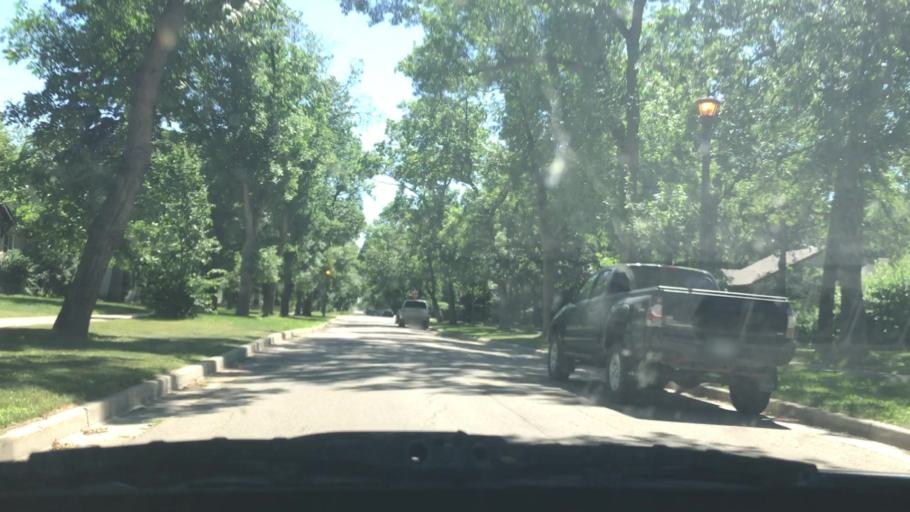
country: CA
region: Manitoba
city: Winnipeg
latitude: 49.8718
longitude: -97.1958
